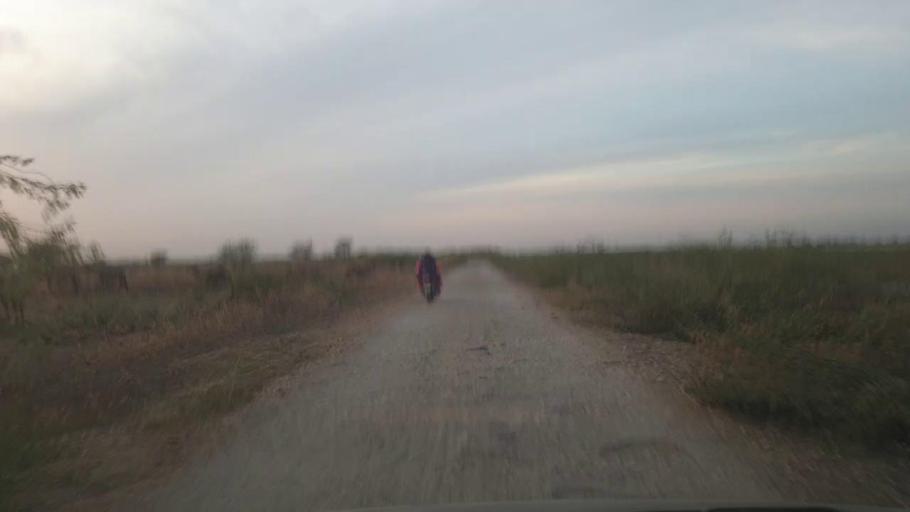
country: PK
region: Sindh
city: Kunri
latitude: 25.2308
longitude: 69.5317
